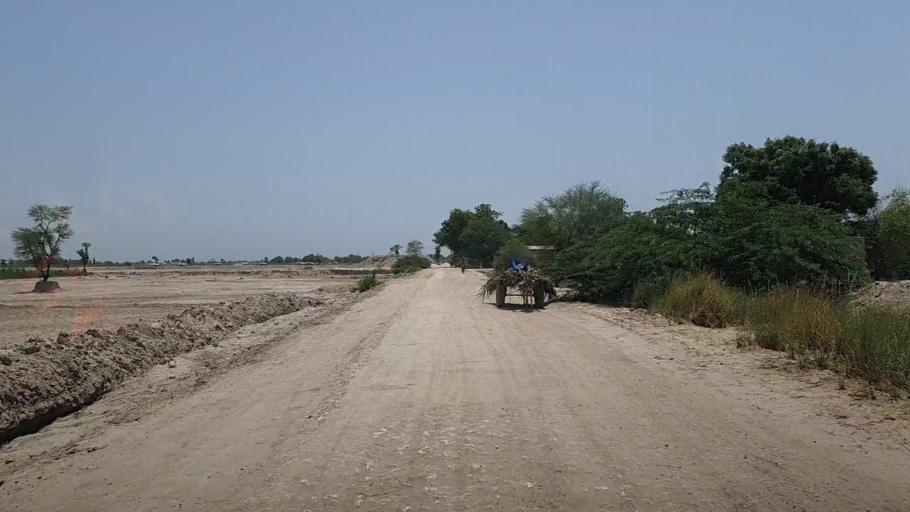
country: PK
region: Sindh
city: Pad Idan
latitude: 26.7665
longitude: 68.2936
